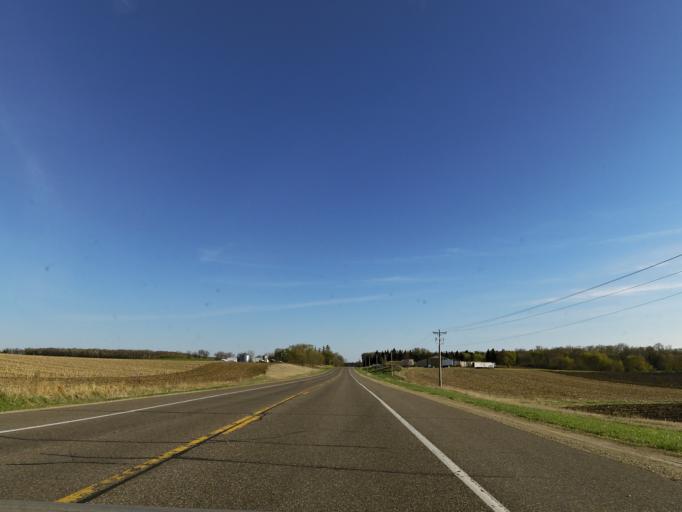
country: US
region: Minnesota
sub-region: Dakota County
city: Lakeville
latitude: 44.5759
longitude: -93.2076
